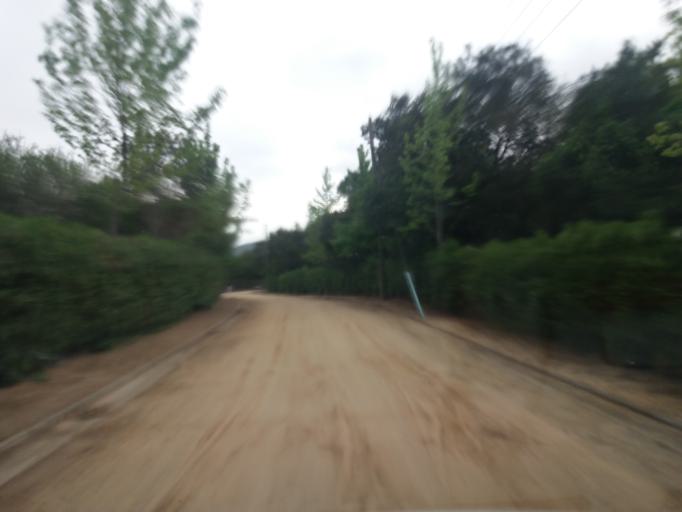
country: CL
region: Valparaiso
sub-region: Provincia de Marga Marga
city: Limache
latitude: -33.0252
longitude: -71.1374
